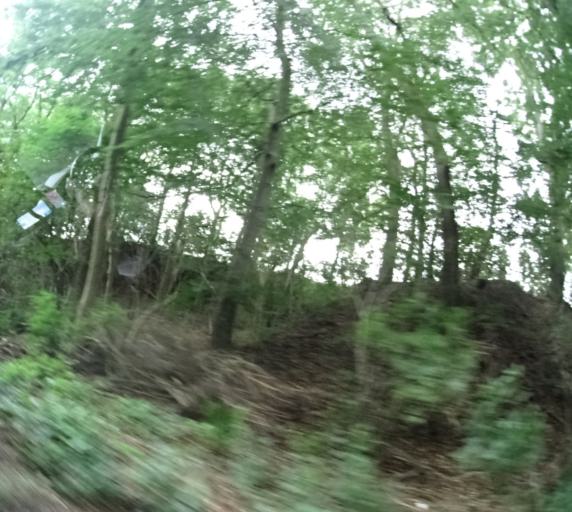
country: DK
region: Central Jutland
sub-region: Syddjurs Kommune
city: Ryomgard
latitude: 56.4071
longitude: 10.5581
